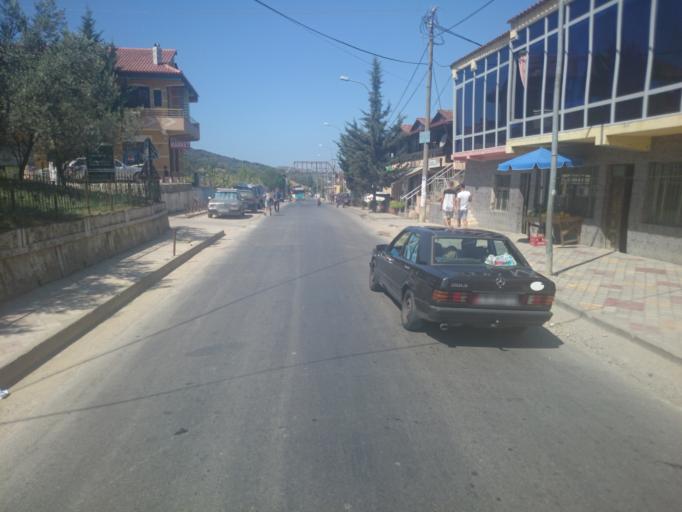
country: AL
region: Tirane
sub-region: Rrethi i Tiranes
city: Ndroq
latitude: 41.2646
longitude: 19.6535
